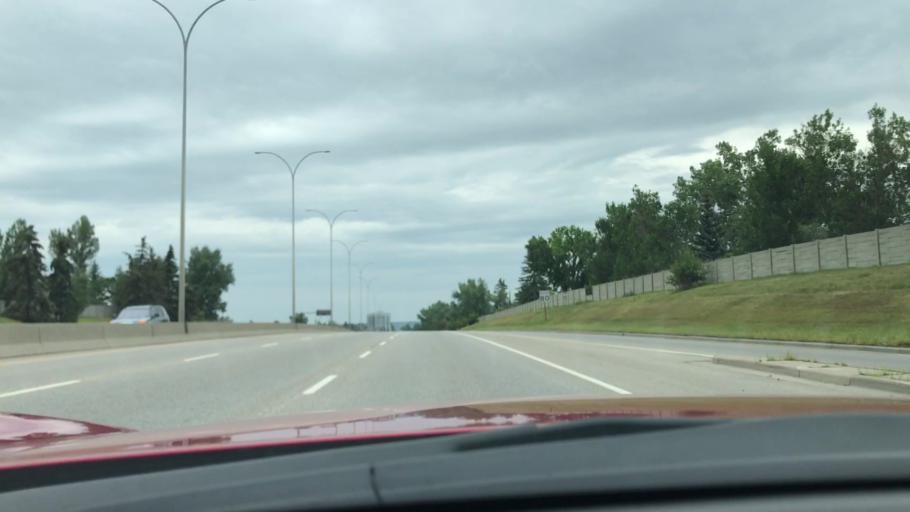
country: CA
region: Alberta
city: Calgary
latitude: 51.0253
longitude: -114.1177
